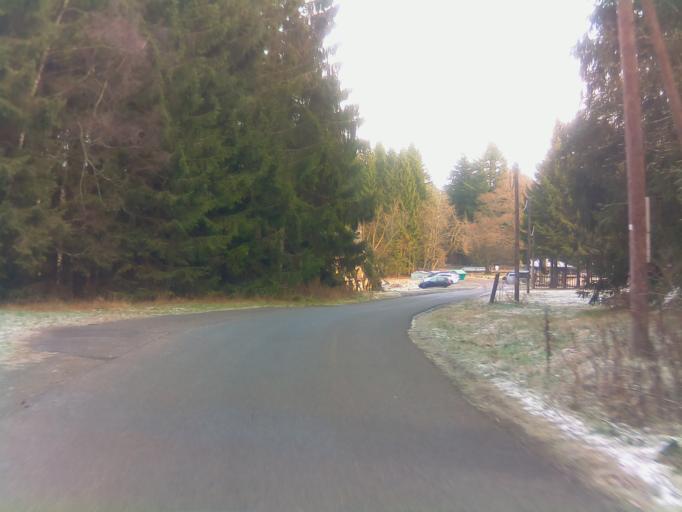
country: DE
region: Thuringia
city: Tabarz
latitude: 50.8419
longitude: 10.5216
